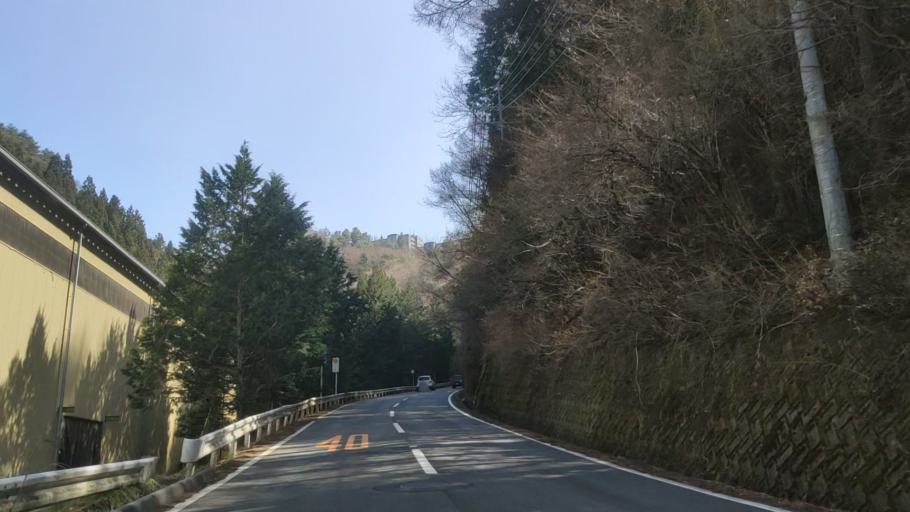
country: JP
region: Yamanashi
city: Fujikawaguchiko
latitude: 35.4619
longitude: 138.8184
